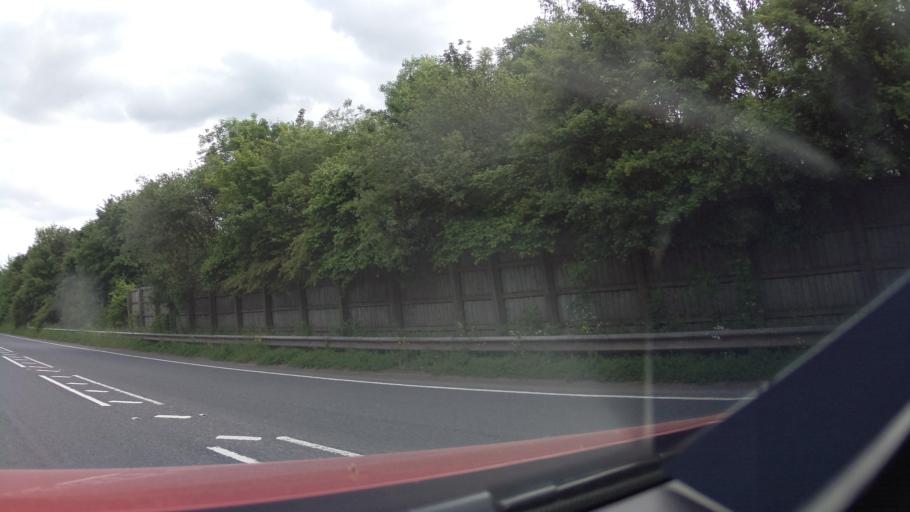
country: GB
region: England
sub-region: Worcestershire
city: Bransford
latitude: 52.1852
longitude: -2.2634
